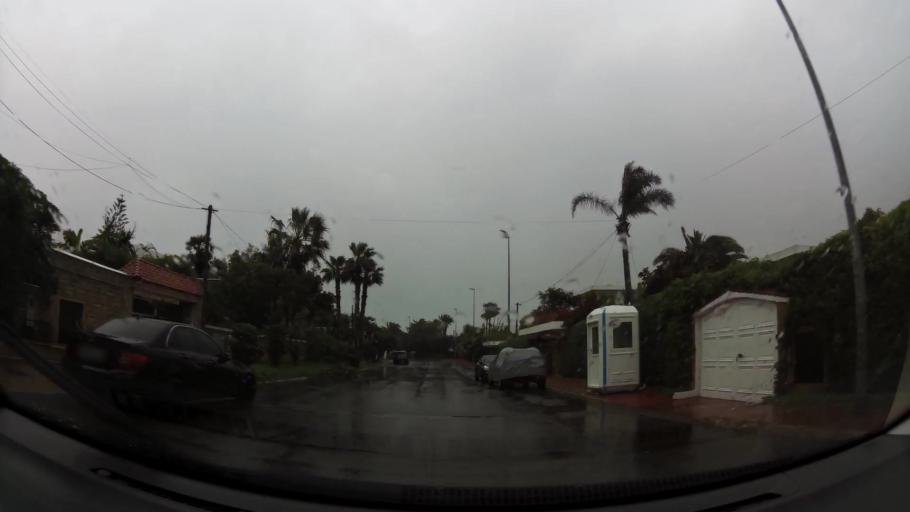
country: MA
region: Grand Casablanca
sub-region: Casablanca
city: Casablanca
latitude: 33.5931
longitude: -7.6683
